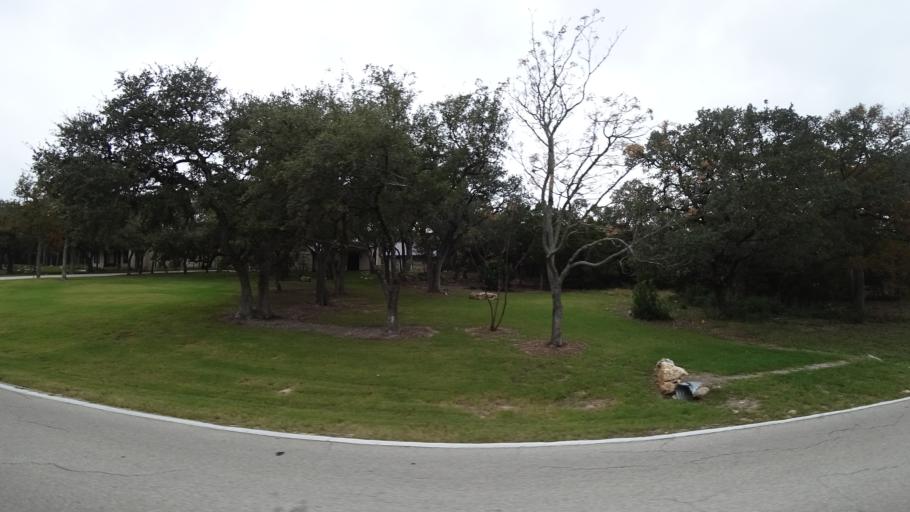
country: US
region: Texas
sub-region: Williamson County
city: Anderson Mill
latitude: 30.4464
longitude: -97.8290
